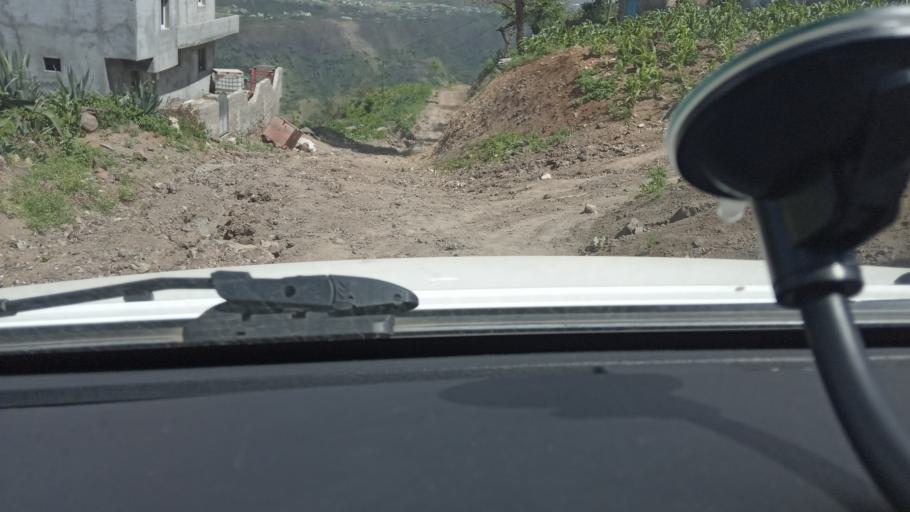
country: CV
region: Santa Catarina
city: Assomada
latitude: 15.0694
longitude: -23.6887
